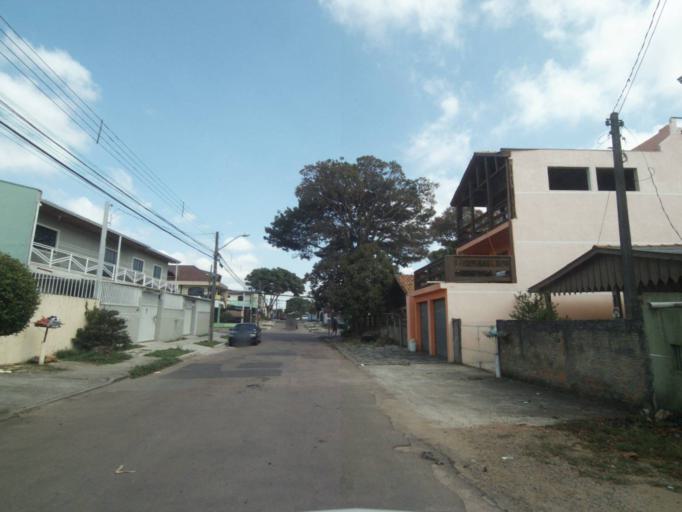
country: BR
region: Parana
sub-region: Sao Jose Dos Pinhais
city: Sao Jose dos Pinhais
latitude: -25.5433
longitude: -49.2651
